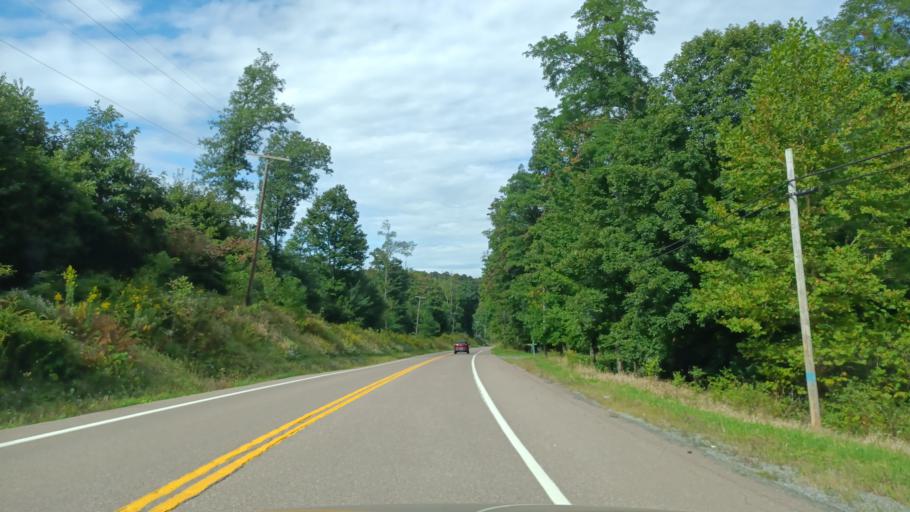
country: US
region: Maryland
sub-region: Garrett County
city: Mountain Lake Park
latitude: 39.2963
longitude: -79.4295
